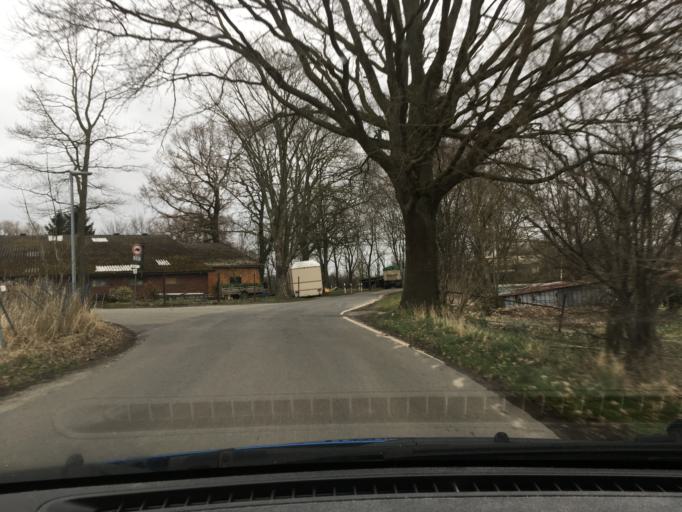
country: DE
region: Lower Saxony
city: Winsen
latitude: 53.3745
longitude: 10.2432
